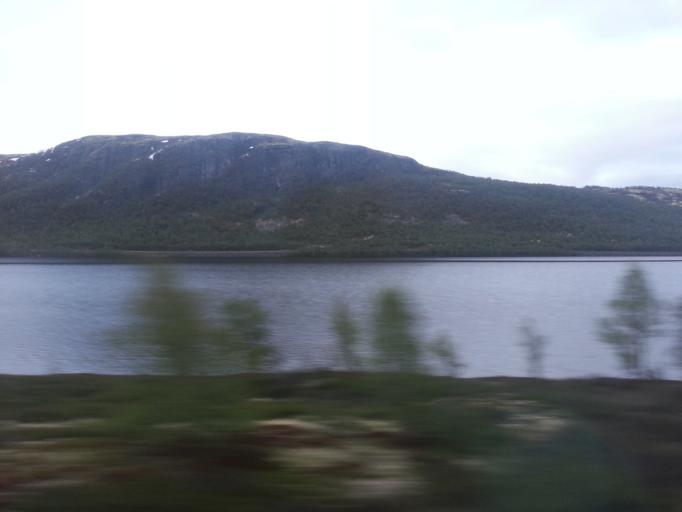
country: NO
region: Oppland
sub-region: Dovre
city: Dovre
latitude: 62.1771
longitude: 9.3959
